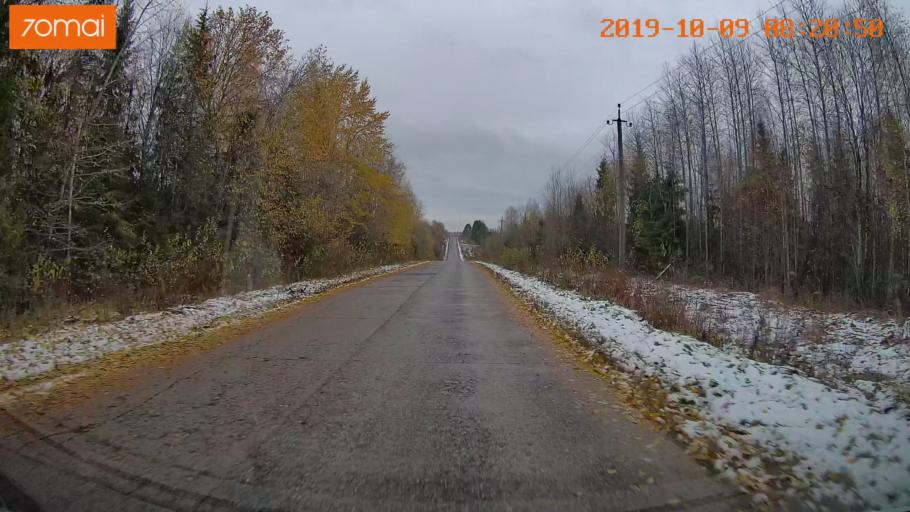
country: RU
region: Vologda
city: Gryazovets
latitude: 58.7425
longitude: 40.2663
